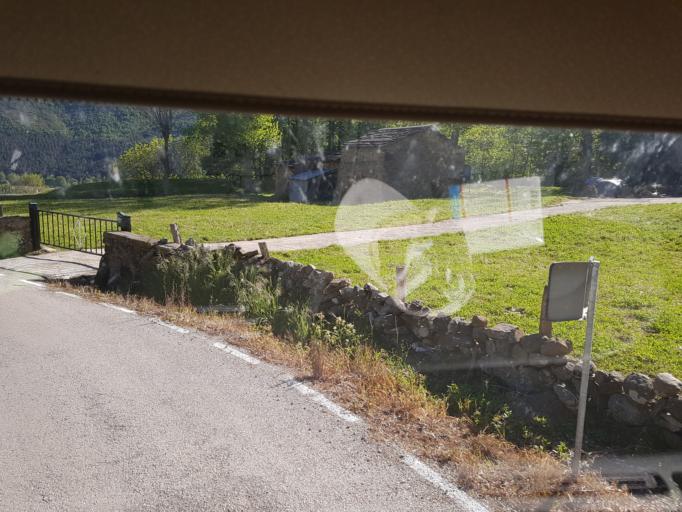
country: ES
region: Castille and Leon
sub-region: Provincia de Burgos
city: Espinosa de los Monteros
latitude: 43.1241
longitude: -3.5791
